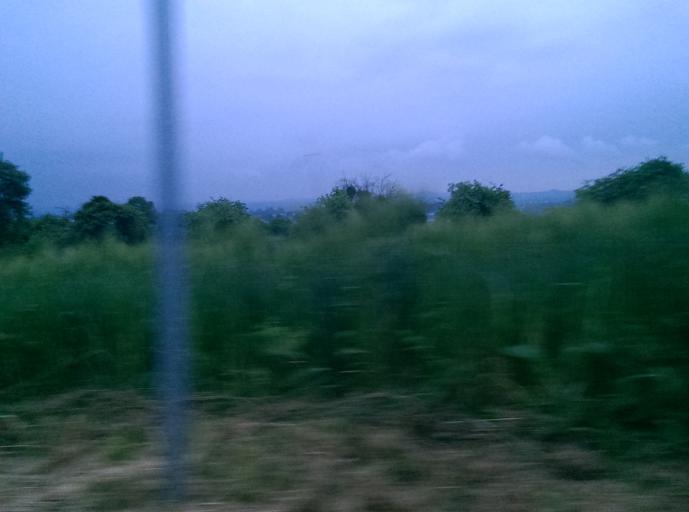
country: DE
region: Rheinland-Pfalz
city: Melsbach
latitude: 50.4747
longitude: 7.4806
